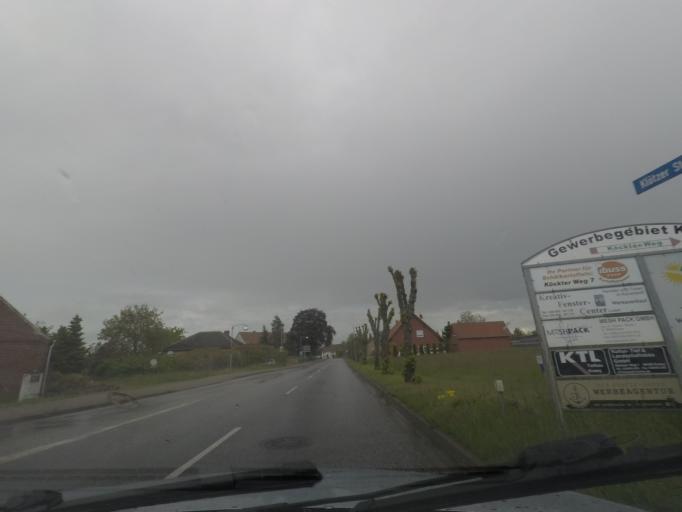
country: DE
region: Saxony-Anhalt
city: Kusey
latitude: 52.5772
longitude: 11.0900
